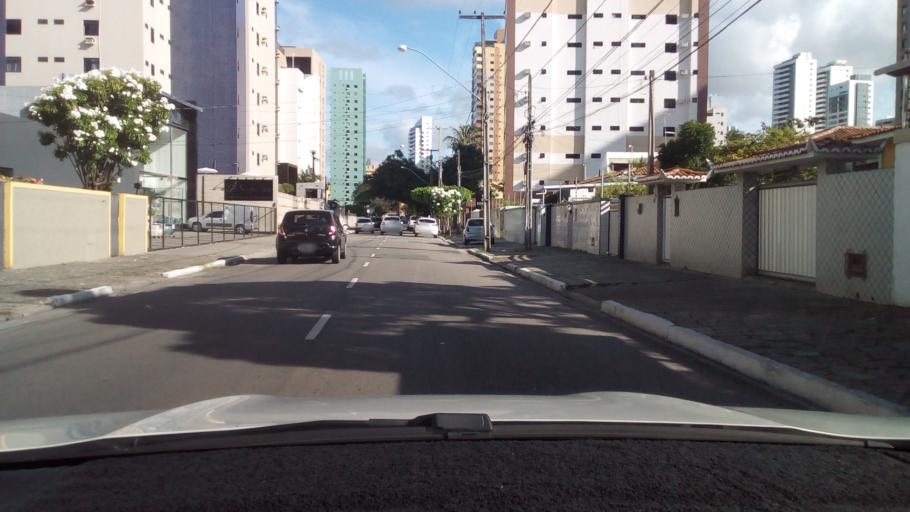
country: BR
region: Paraiba
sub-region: Joao Pessoa
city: Joao Pessoa
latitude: -7.1035
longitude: -34.8353
